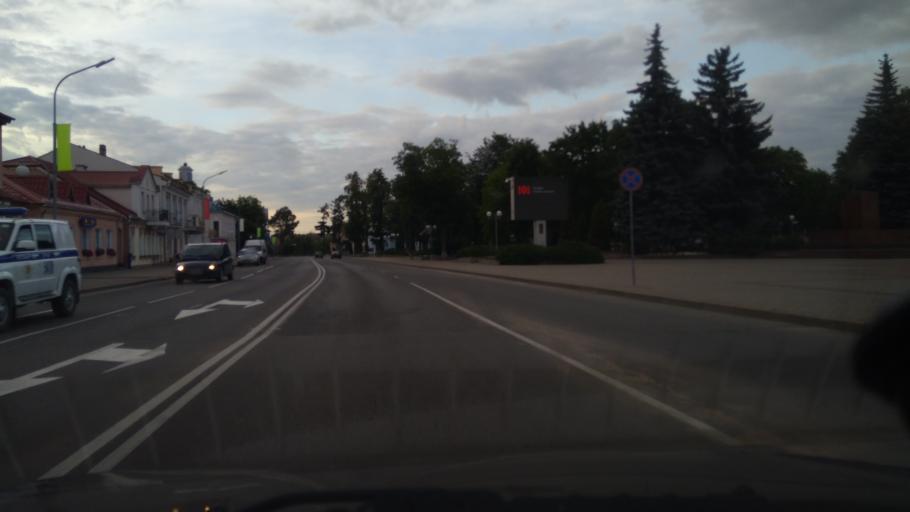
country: BY
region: Grodnenskaya
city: Shchuchin
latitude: 53.6042
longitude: 24.7420
